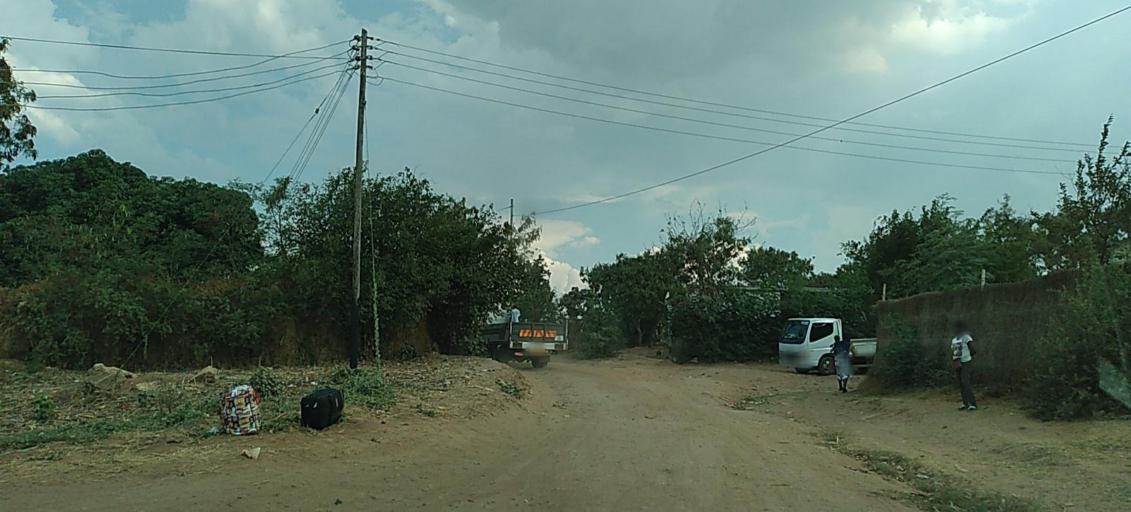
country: ZM
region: Lusaka
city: Lusaka
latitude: -15.5417
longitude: 28.2418
